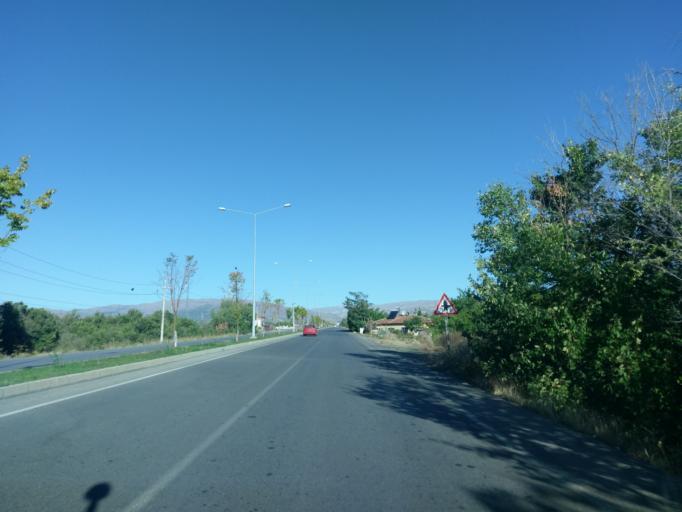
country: TR
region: Erzincan
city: Erzincan
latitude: 39.7746
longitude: 39.4192
